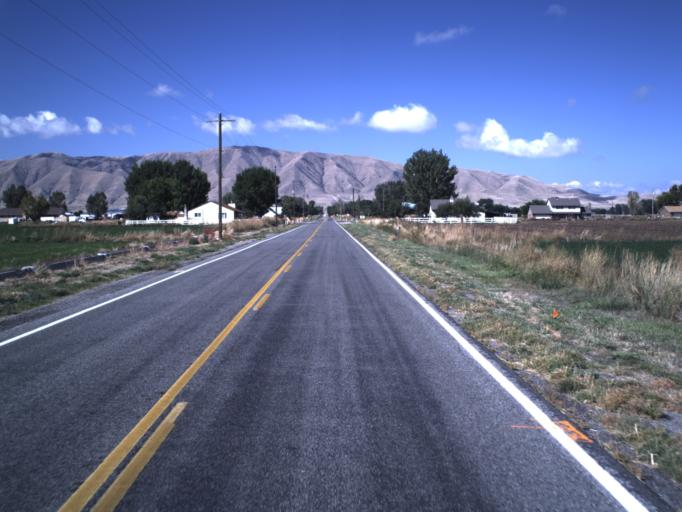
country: US
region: Utah
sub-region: Utah County
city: Benjamin
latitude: 40.0983
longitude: -111.7135
